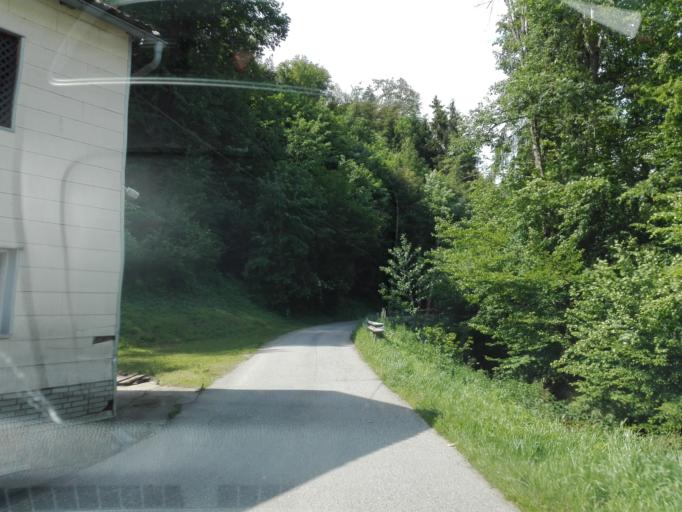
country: AT
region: Upper Austria
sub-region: Politischer Bezirk Perg
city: Perg
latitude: 48.2337
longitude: 14.6873
